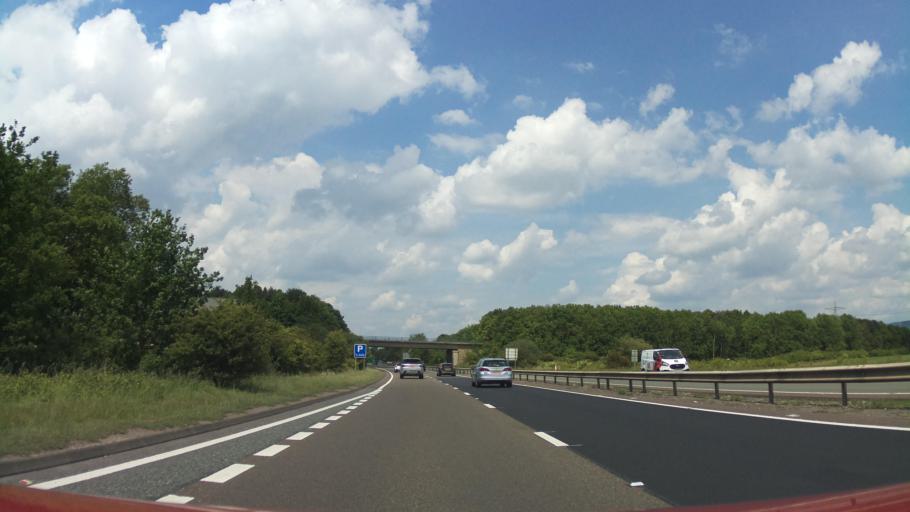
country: GB
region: England
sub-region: North Yorkshire
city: Thirsk
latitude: 54.2324
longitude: -1.3257
